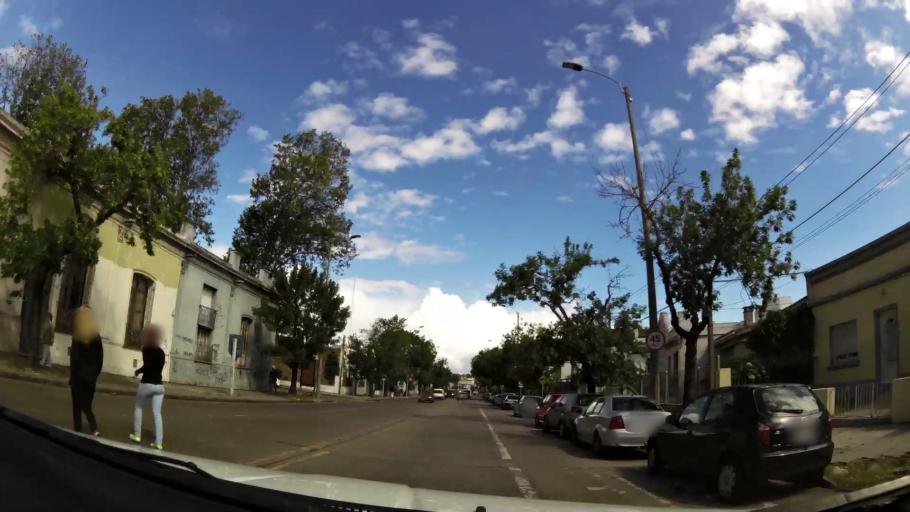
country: UY
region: Montevideo
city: Montevideo
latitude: -34.8610
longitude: -56.1945
